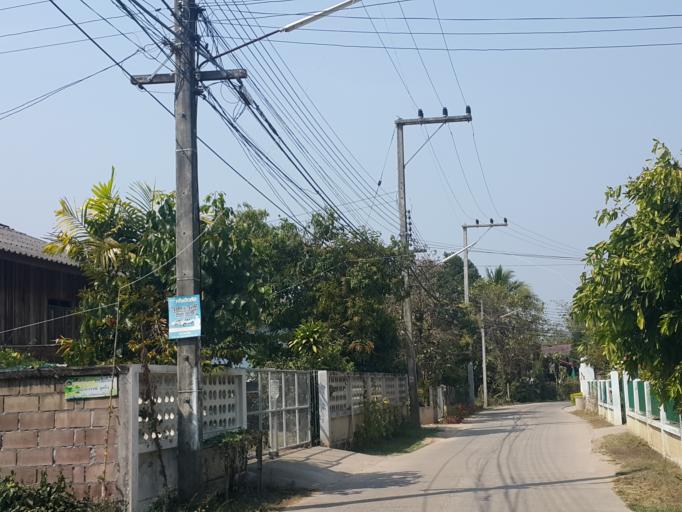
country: TH
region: Chiang Mai
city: San Sai
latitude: 18.9531
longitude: 98.9189
